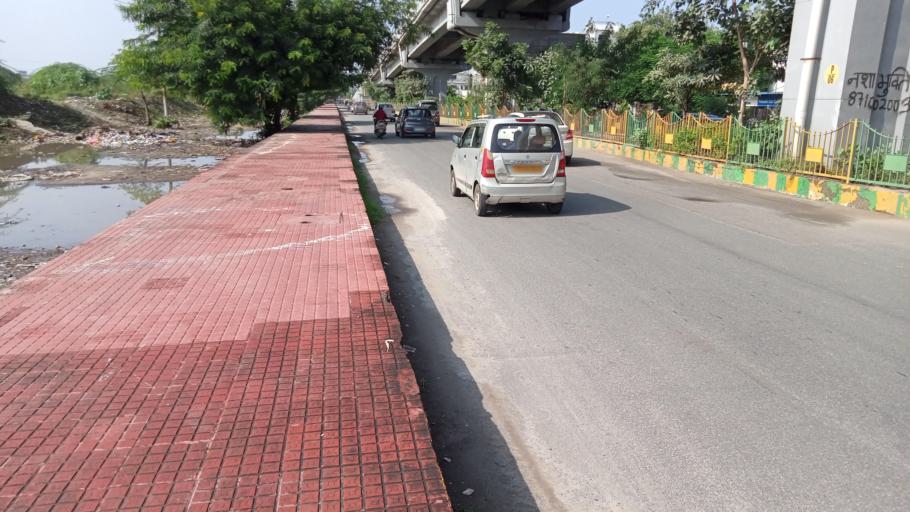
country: IN
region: Uttar Pradesh
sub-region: Ghaziabad
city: Ghaziabad
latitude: 28.6585
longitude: 77.3757
